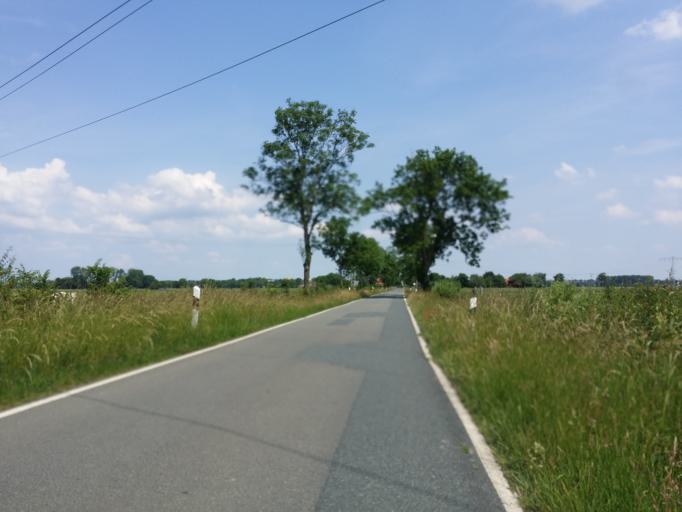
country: DE
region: Lower Saxony
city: Lemwerder
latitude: 53.1460
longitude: 8.5787
